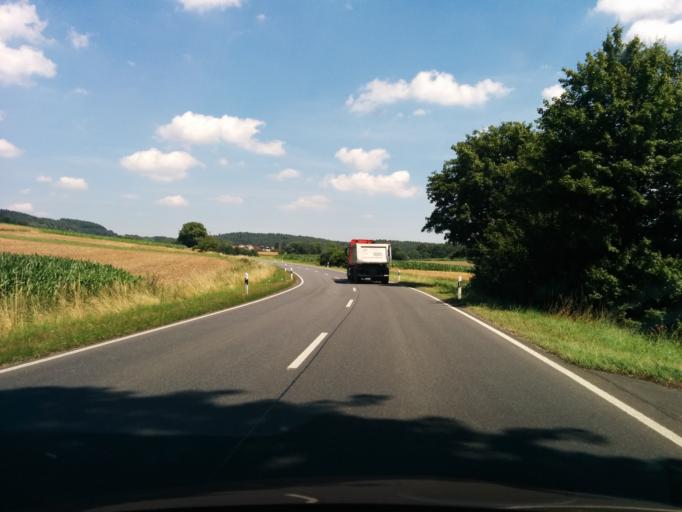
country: DE
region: Hesse
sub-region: Regierungsbezirk Kassel
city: Gilserberg
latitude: 50.9132
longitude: 9.0115
